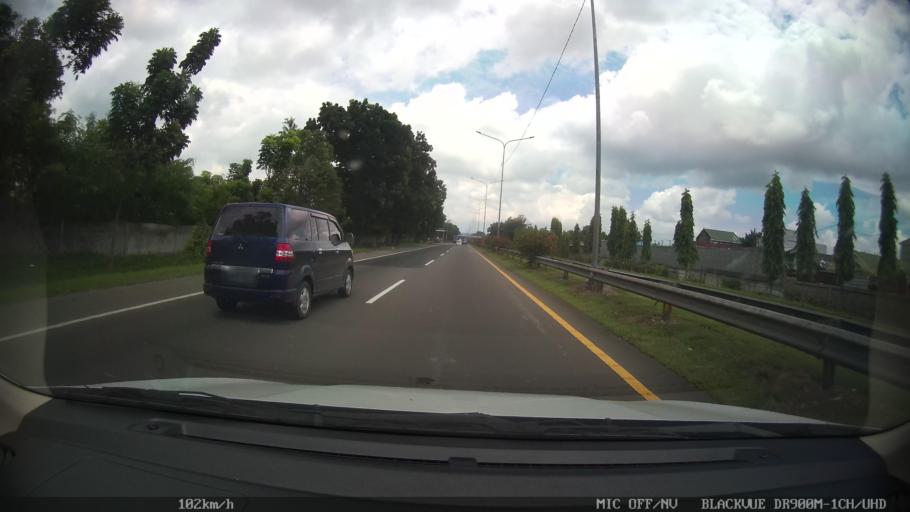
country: ID
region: North Sumatra
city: Medan
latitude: 3.6173
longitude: 98.7208
